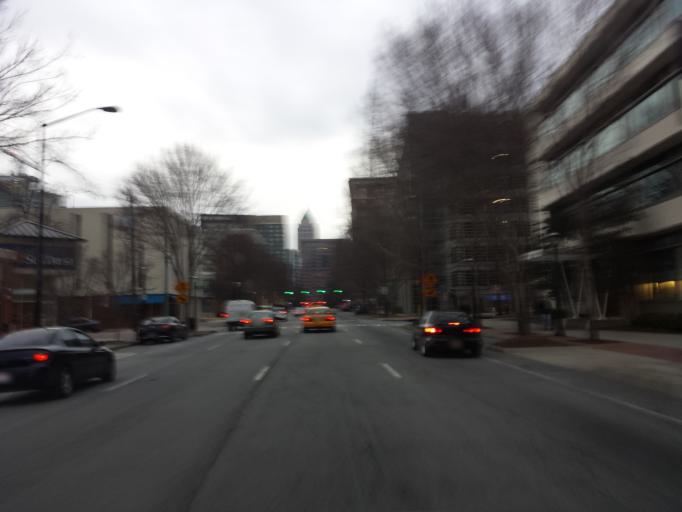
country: US
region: Georgia
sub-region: Fulton County
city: Atlanta
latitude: 33.7746
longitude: -84.3873
